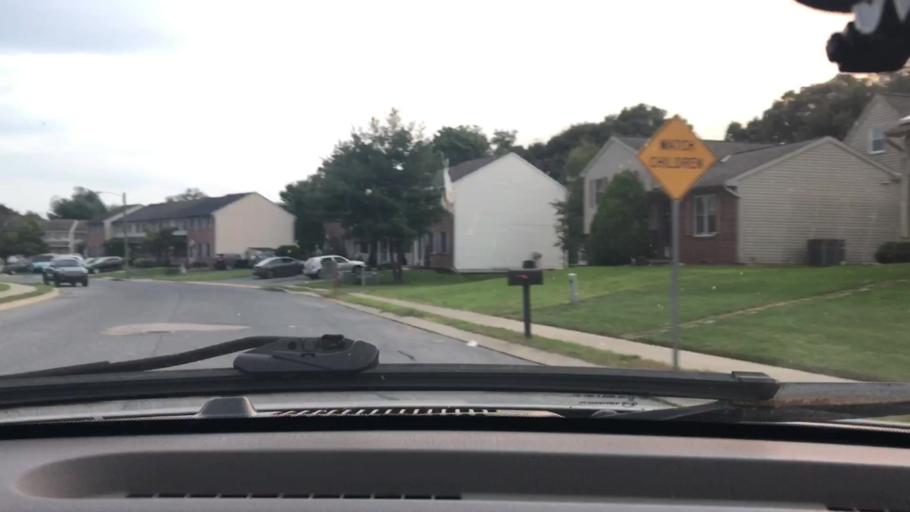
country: US
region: Pennsylvania
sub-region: Lancaster County
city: Elizabethtown
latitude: 40.1624
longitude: -76.5848
